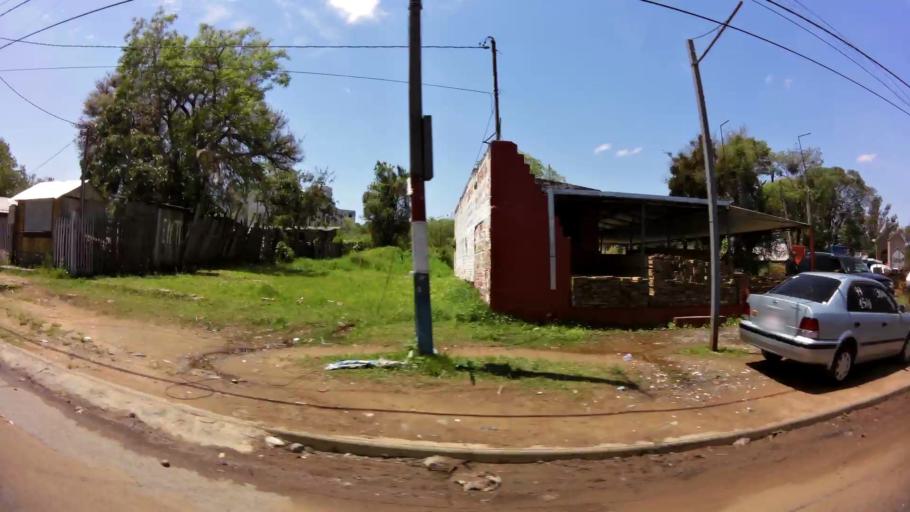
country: PY
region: Central
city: Nemby
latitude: -25.3896
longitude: -57.5473
